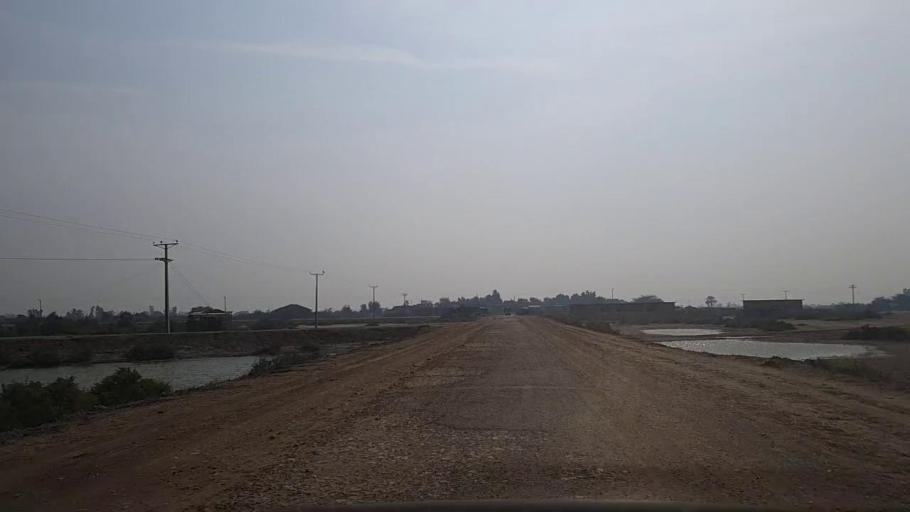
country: PK
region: Sindh
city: Mirpur Sakro
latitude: 24.4046
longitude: 67.7432
